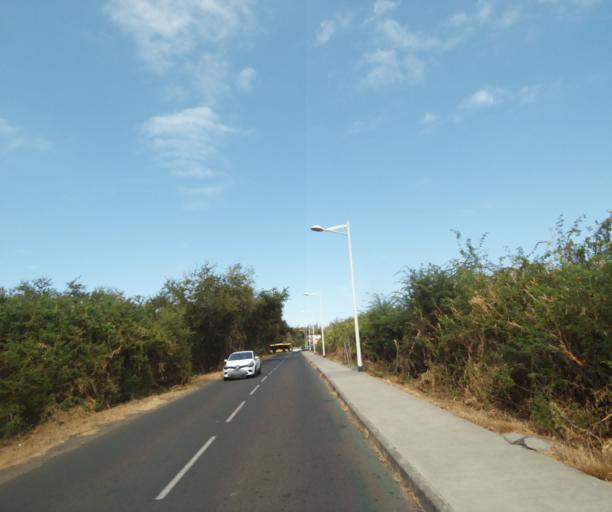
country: RE
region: Reunion
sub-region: Reunion
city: Trois-Bassins
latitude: -21.0843
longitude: 55.2334
